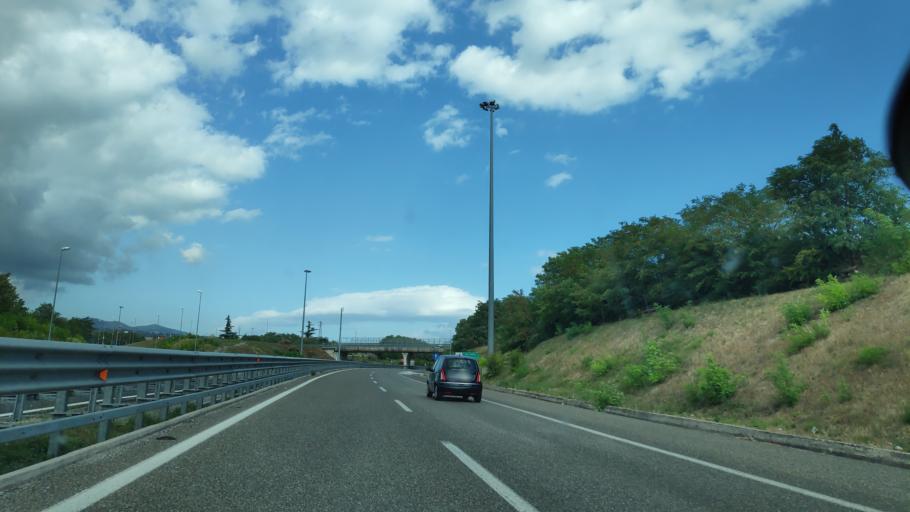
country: IT
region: Campania
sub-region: Provincia di Salerno
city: Palomonte
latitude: 40.6101
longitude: 15.2909
